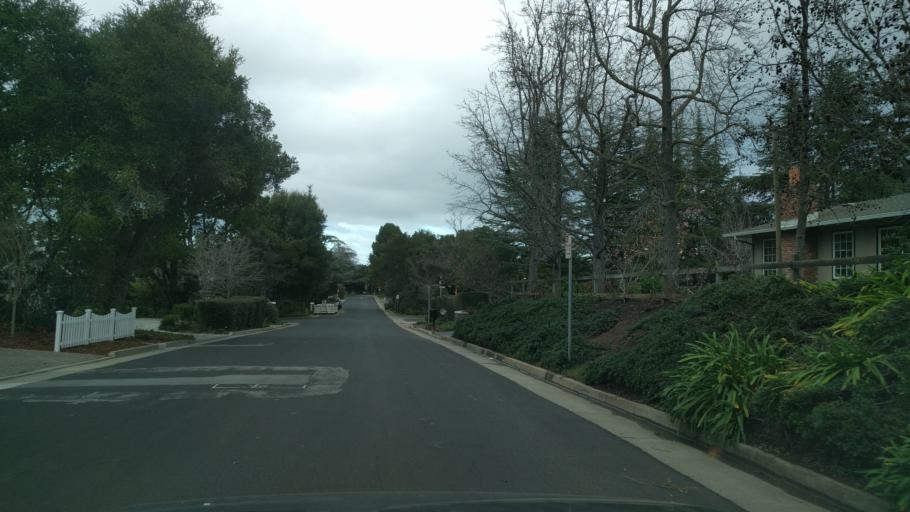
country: US
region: California
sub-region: Santa Clara County
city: Los Altos Hills
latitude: 37.3952
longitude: -122.1333
